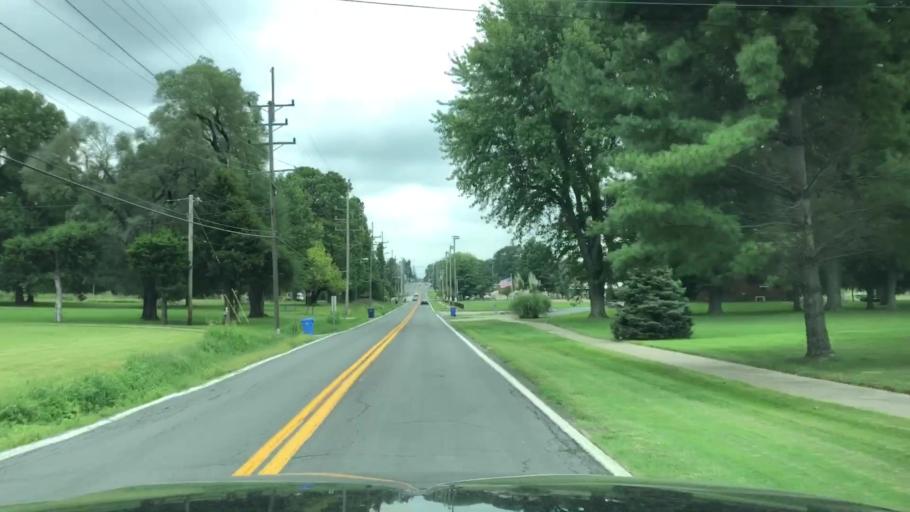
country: US
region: Missouri
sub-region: Saint Louis County
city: Hazelwood
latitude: 38.8127
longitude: -90.3652
